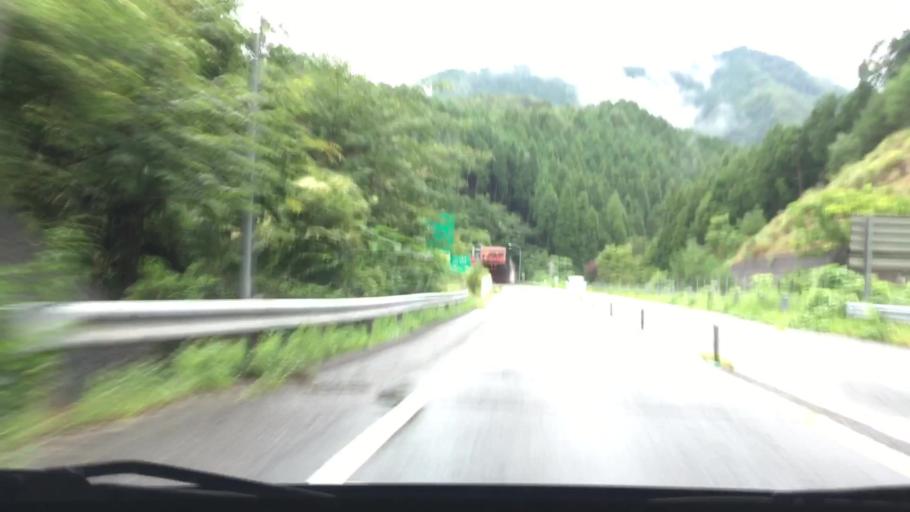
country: JP
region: Hyogo
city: Toyooka
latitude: 35.2407
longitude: 134.7861
